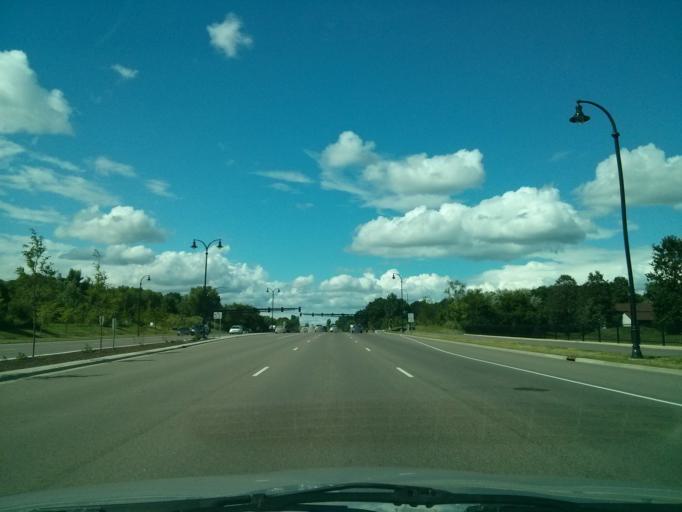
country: US
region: Minnesota
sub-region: Dakota County
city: Apple Valley
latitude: 44.7447
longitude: -93.2175
